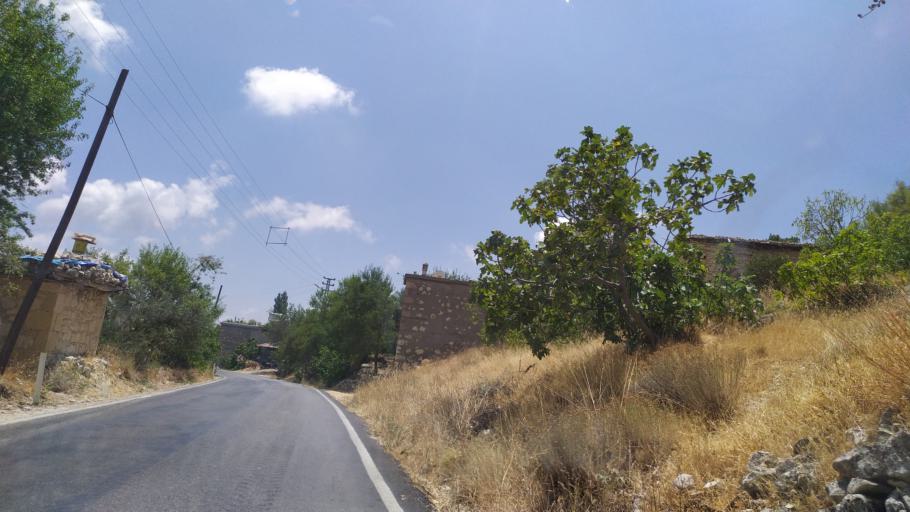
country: TR
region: Mersin
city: Gulnar
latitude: 36.2860
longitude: 33.3834
